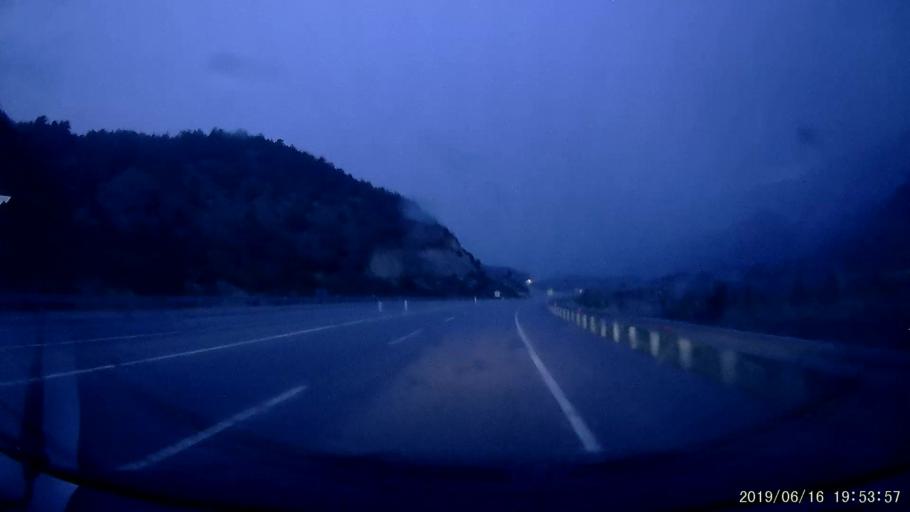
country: TR
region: Sivas
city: Koyulhisar
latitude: 40.2894
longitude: 37.7748
